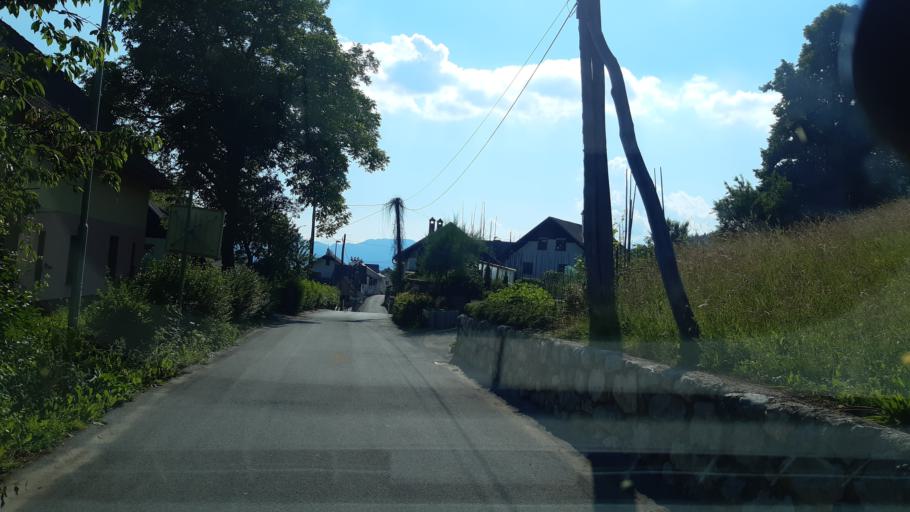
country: SI
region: Radovljica
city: Radovljica
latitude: 46.3789
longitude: 14.2092
